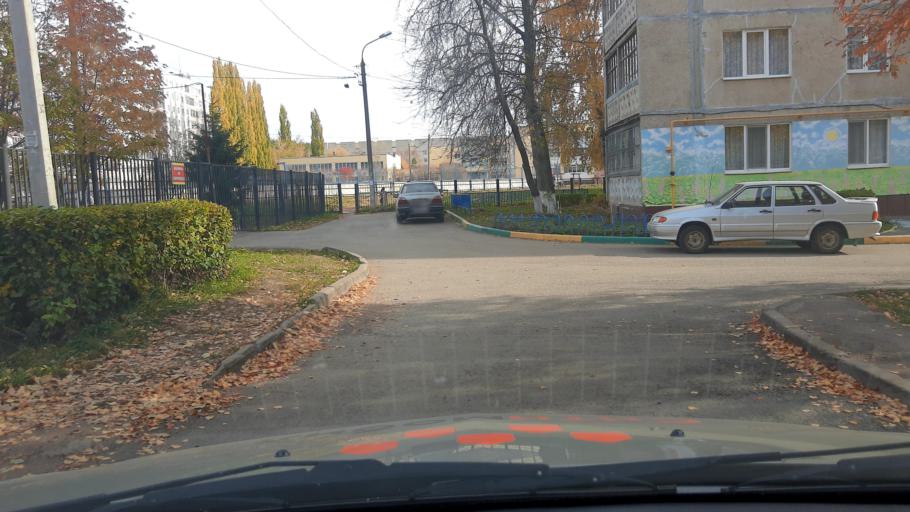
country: RU
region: Bashkortostan
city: Ufa
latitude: 54.7044
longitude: 56.0030
